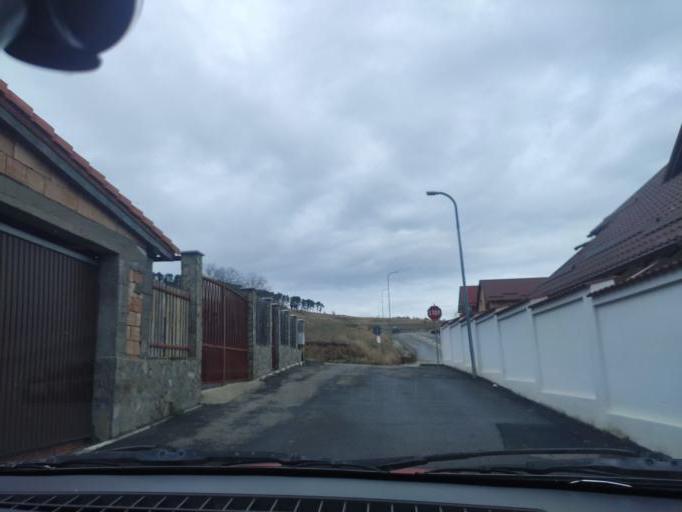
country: RO
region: Brasov
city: Codlea
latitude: 45.7063
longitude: 25.4415
